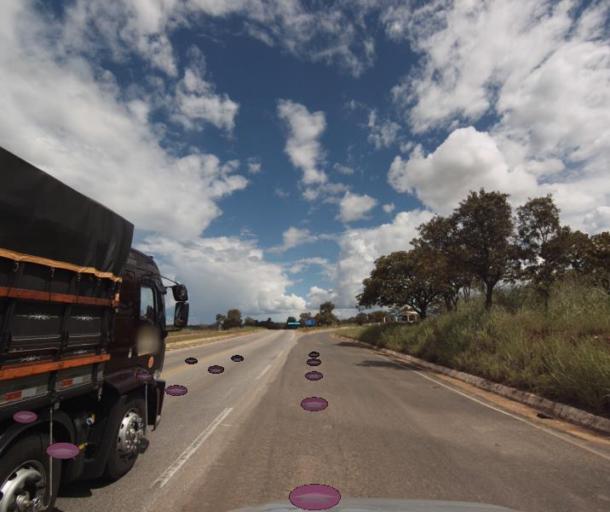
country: BR
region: Goias
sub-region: Porangatu
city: Porangatu
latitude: -13.8649
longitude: -49.0512
